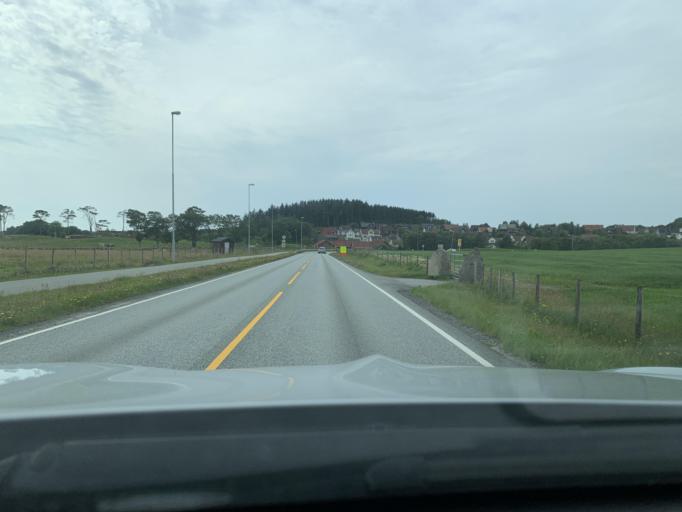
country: NO
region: Rogaland
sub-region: Time
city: Bryne
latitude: 58.7340
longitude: 5.6817
